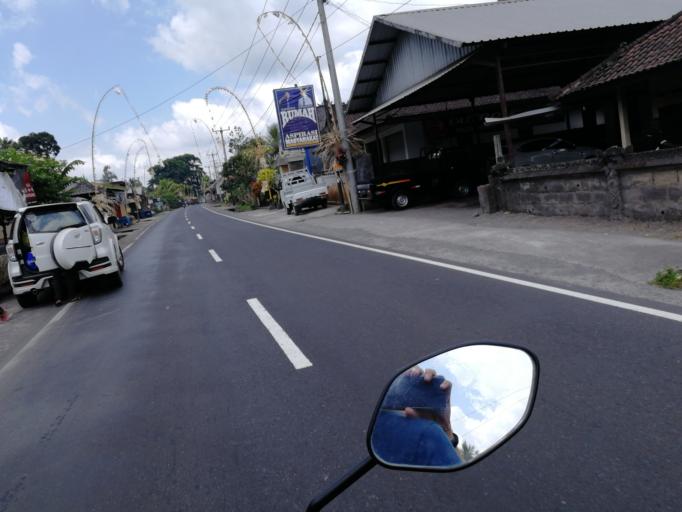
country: ID
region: Bali
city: Banjar Wangsian
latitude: -8.4285
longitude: 115.4323
